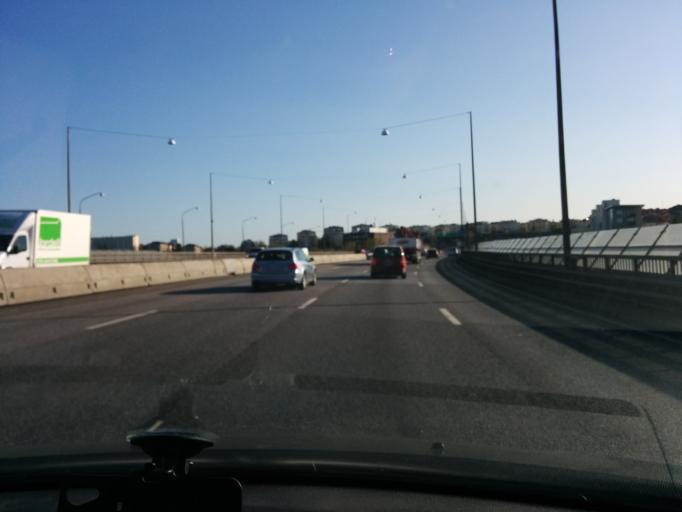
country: SE
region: Stockholm
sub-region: Solna Kommun
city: Solna
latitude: 59.3224
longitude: 17.9975
